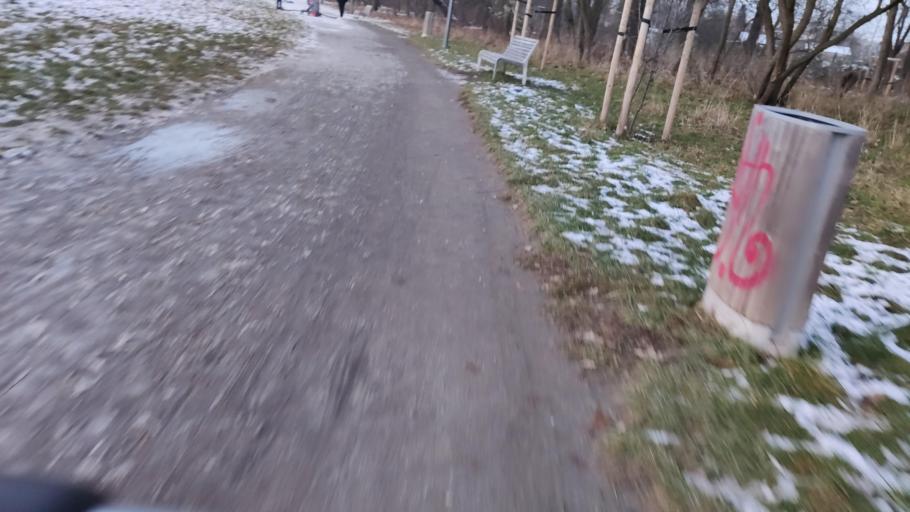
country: PL
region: Lower Silesian Voivodeship
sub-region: Powiat wroclawski
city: Wroclaw
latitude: 51.0843
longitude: 16.9950
